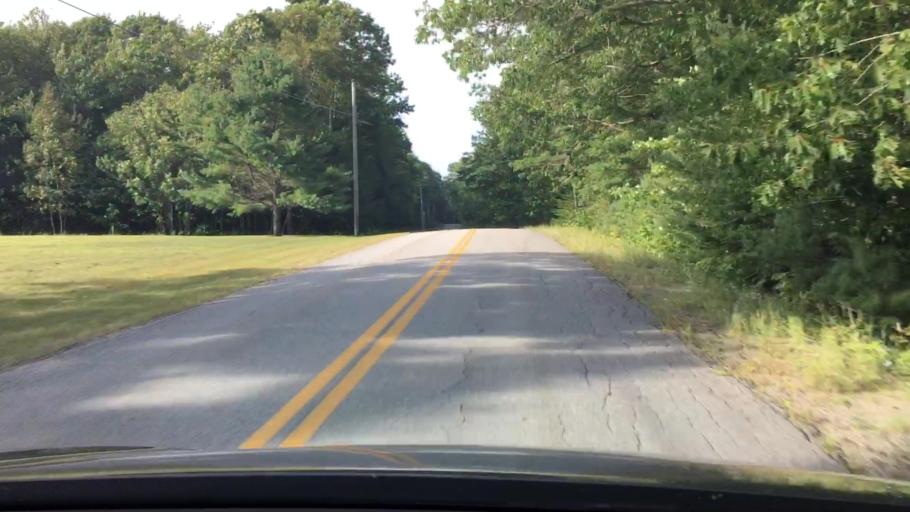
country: US
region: Maine
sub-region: Hancock County
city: Orland
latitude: 44.5254
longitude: -68.7639
